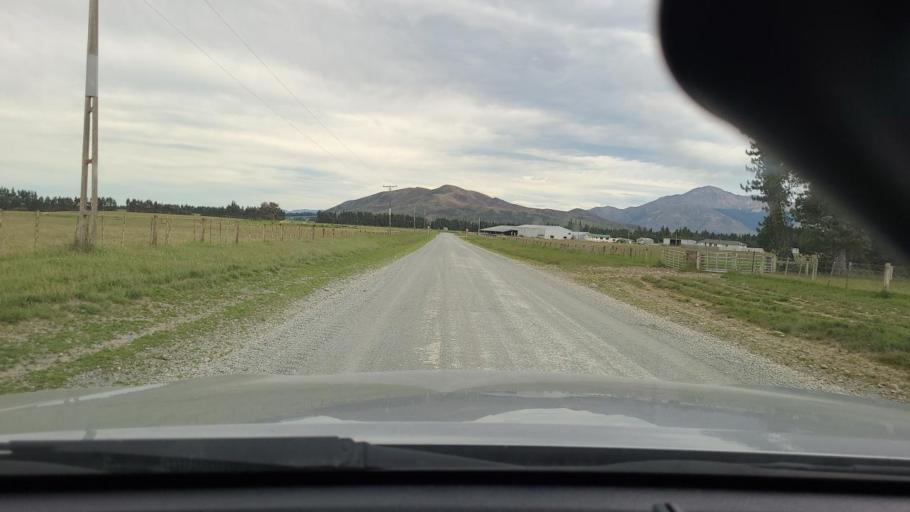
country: NZ
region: Southland
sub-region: Southland District
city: Te Anau
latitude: -45.5331
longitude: 168.1201
